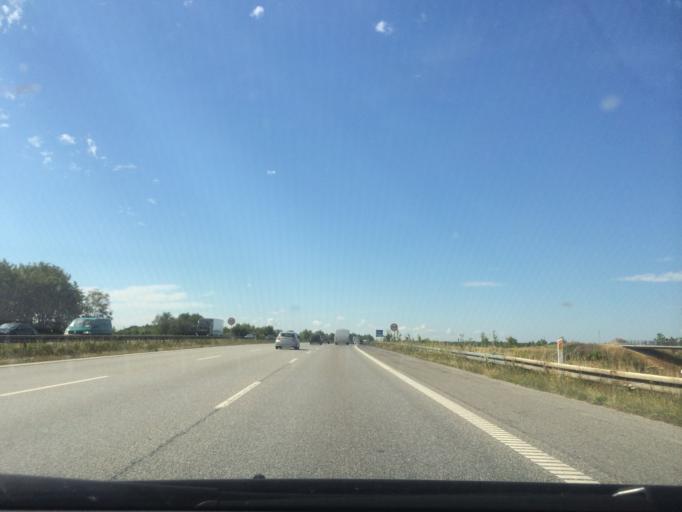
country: DK
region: Zealand
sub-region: Koge Kommune
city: Koge
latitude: 55.4928
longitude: 12.1704
